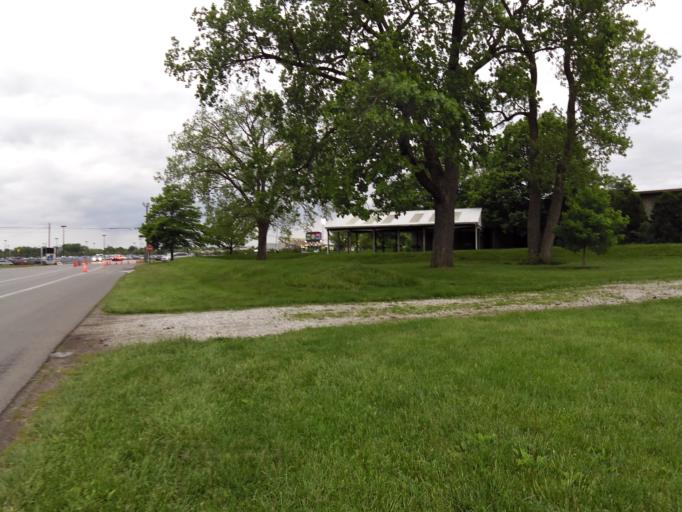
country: US
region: Ohio
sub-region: Franklin County
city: Columbus
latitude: 40.0041
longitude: -82.9883
